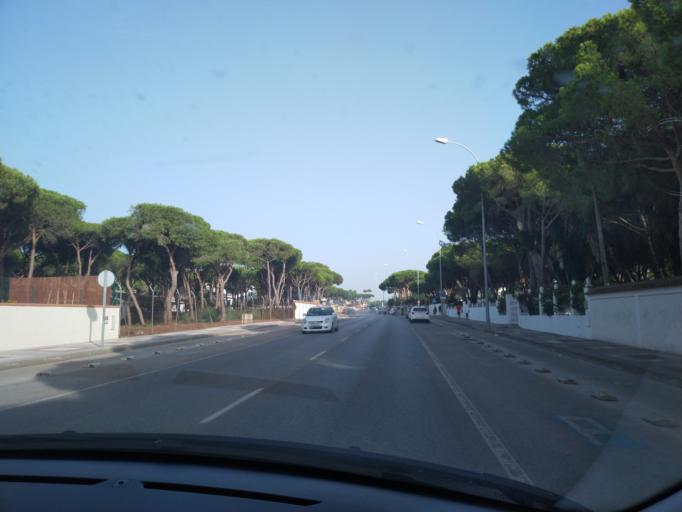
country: ES
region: Andalusia
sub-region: Provincia de Cadiz
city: Chiclana de la Frontera
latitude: 36.3782
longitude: -6.1890
